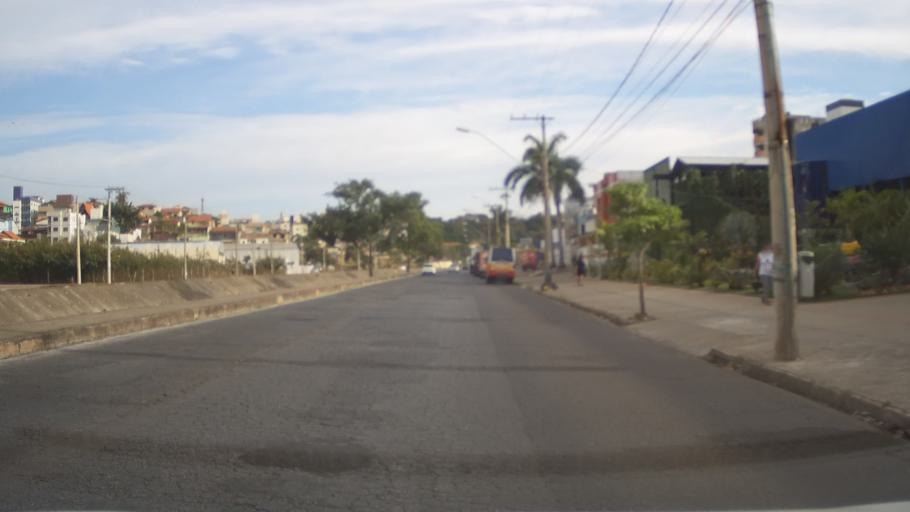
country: BR
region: Minas Gerais
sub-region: Contagem
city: Contagem
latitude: -19.8820
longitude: -44.0058
